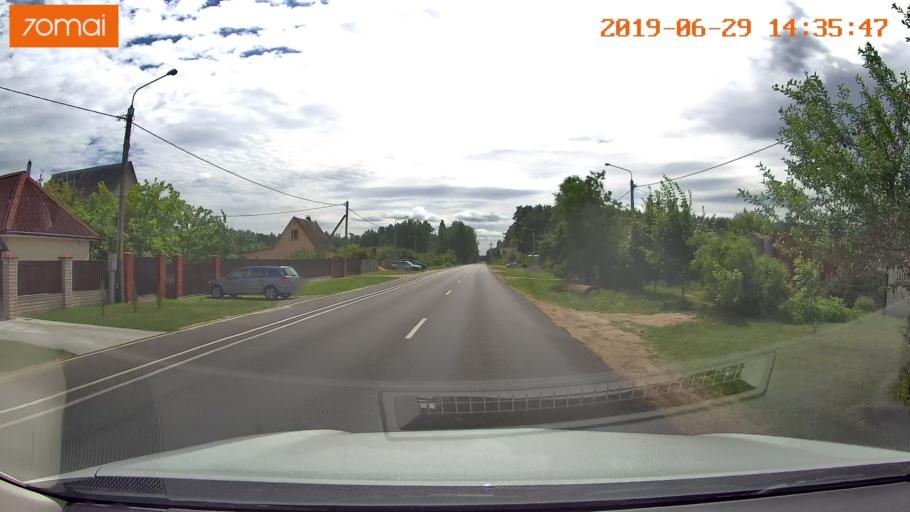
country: BY
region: Minsk
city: Starobin
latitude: 52.7572
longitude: 27.4836
